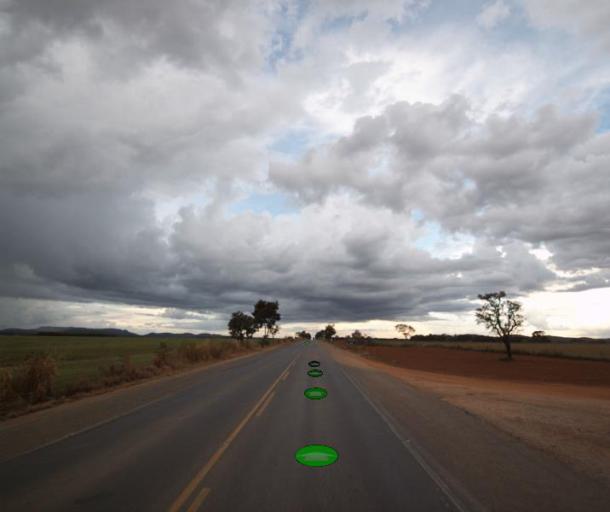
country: BR
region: Goias
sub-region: Uruacu
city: Uruacu
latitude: -14.7714
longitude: -49.2664
